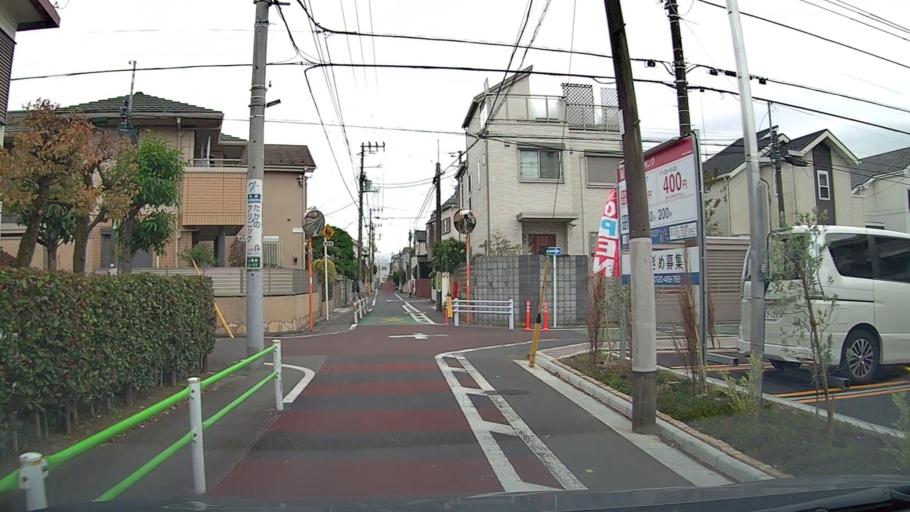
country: JP
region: Saitama
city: Wako
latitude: 35.7304
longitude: 139.6326
